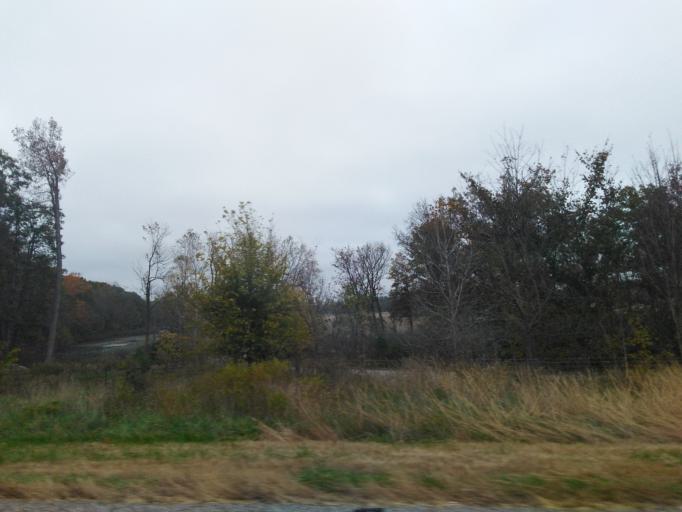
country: US
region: Illinois
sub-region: Bond County
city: Greenville
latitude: 38.8341
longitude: -89.5266
